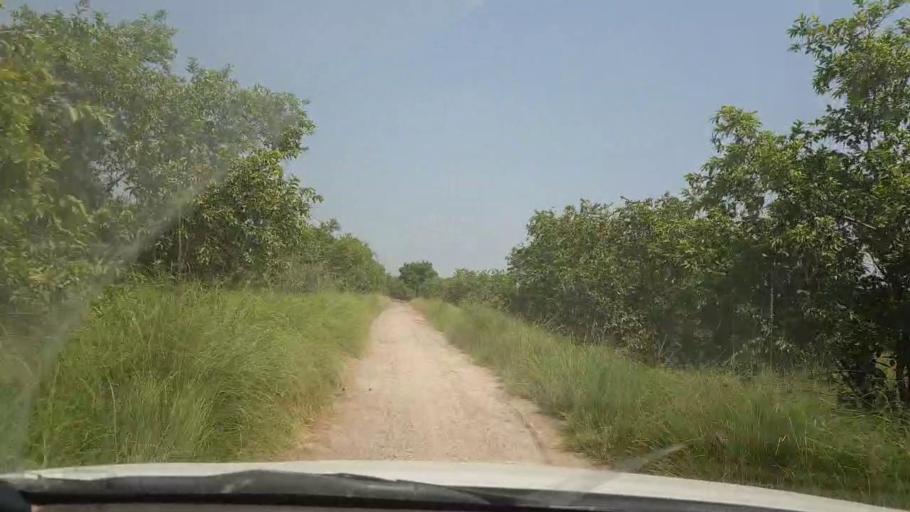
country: PK
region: Sindh
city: Lakhi
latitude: 27.8634
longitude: 68.6984
